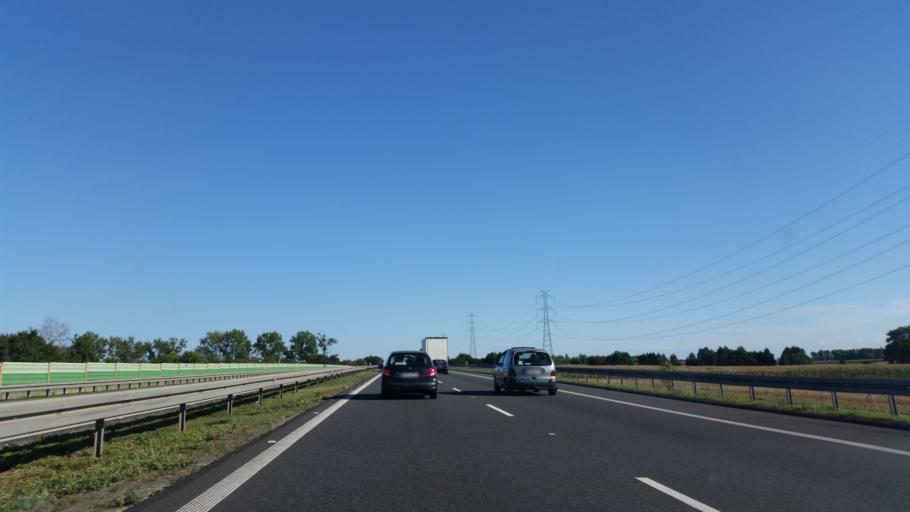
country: PL
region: Opole Voivodeship
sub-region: Powiat brzeski
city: Skarbimierz Osiedle
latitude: 50.8096
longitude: 17.3144
